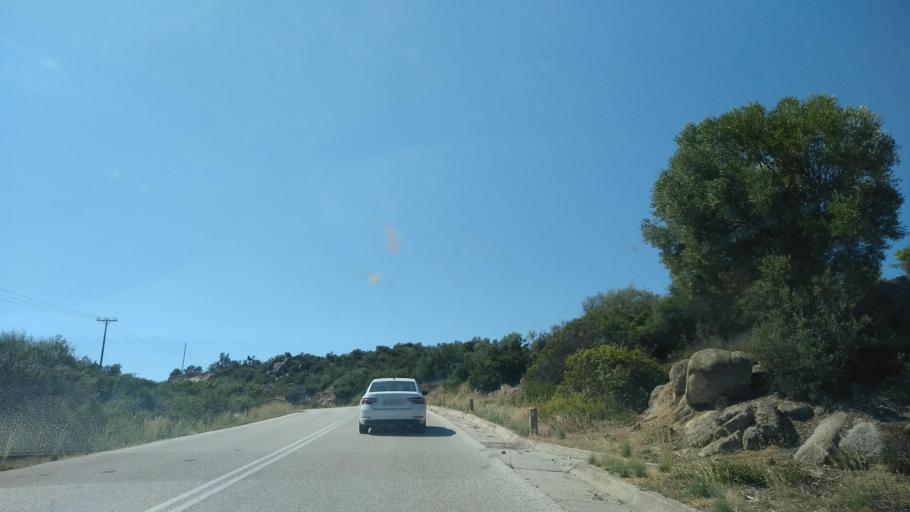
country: GR
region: Central Macedonia
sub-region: Nomos Chalkidikis
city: Sykia
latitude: 39.9953
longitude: 23.8983
